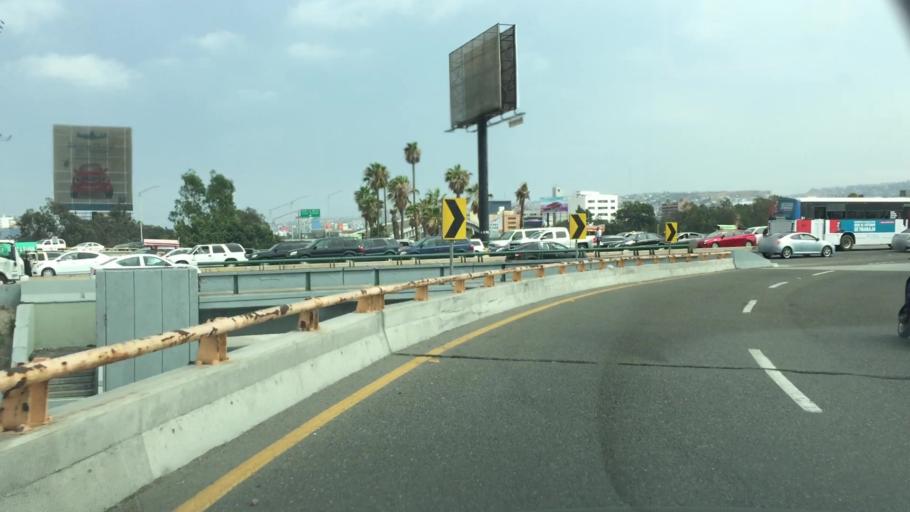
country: MX
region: Baja California
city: Tijuana
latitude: 32.5370
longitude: -117.0285
